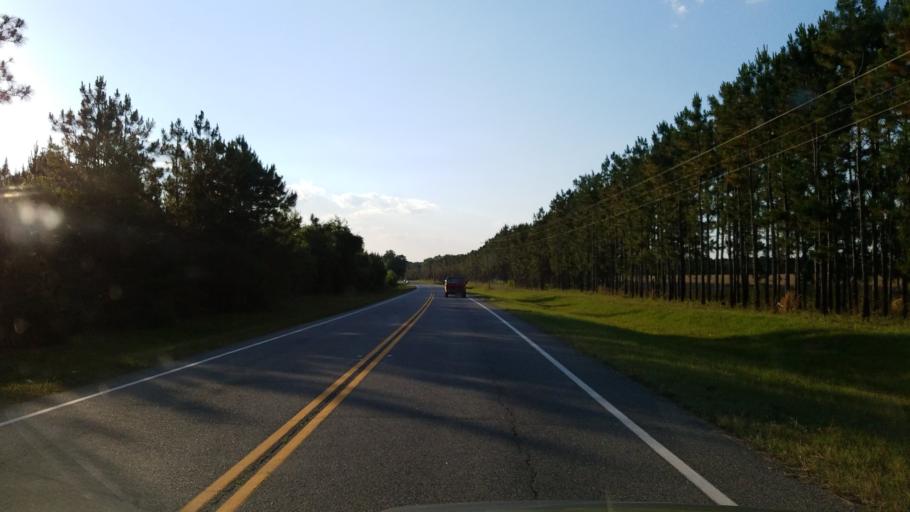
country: US
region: Georgia
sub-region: Berrien County
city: Enigma
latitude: 31.2984
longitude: -83.3513
